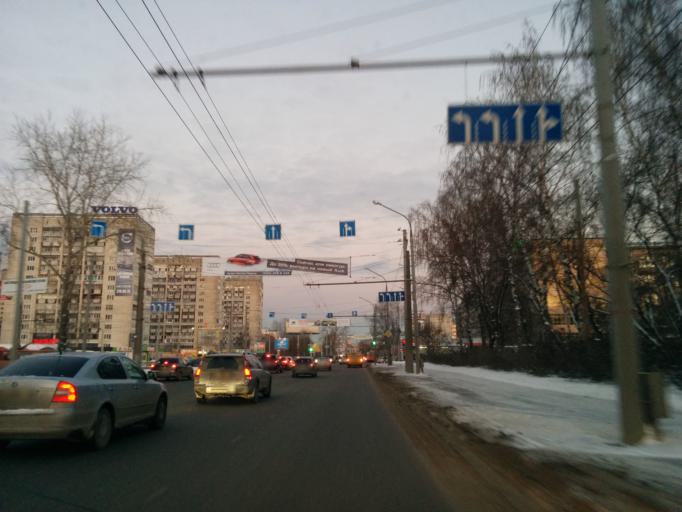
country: RU
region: Perm
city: Perm
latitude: 57.9900
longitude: 56.1932
